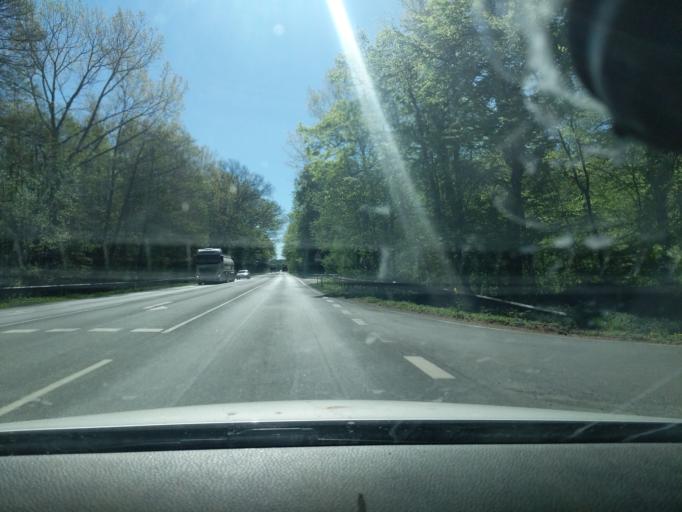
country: DE
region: Lower Saxony
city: Nottensdorf
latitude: 53.4905
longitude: 9.6087
